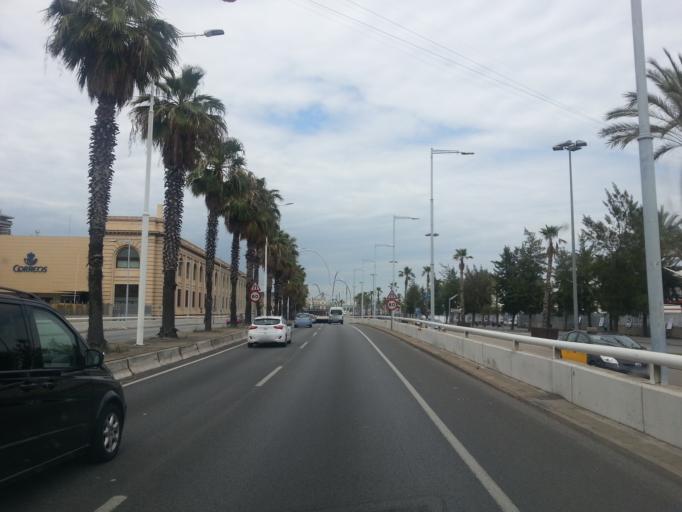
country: ES
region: Catalonia
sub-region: Provincia de Barcelona
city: Ciutat Vella
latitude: 41.3707
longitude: 2.1747
